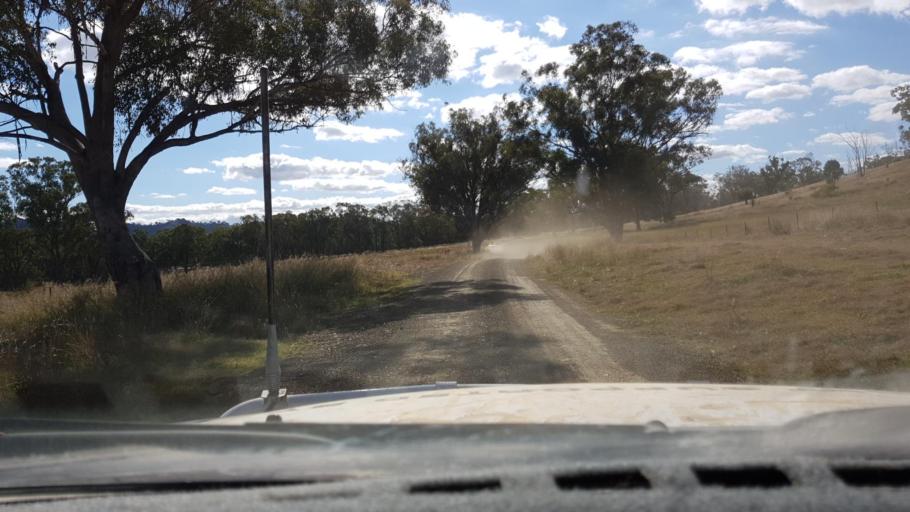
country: AU
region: New South Wales
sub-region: Tamworth Municipality
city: Manilla
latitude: -30.4651
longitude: 150.7784
